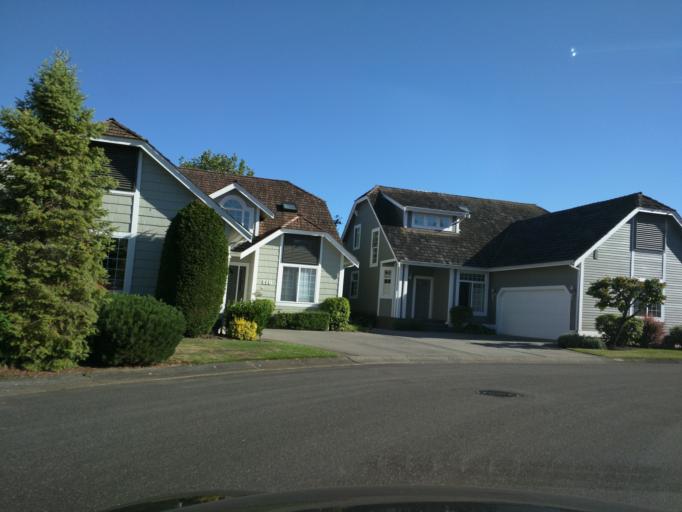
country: US
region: Washington
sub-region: Whatcom County
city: Lynden
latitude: 48.9597
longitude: -122.4472
